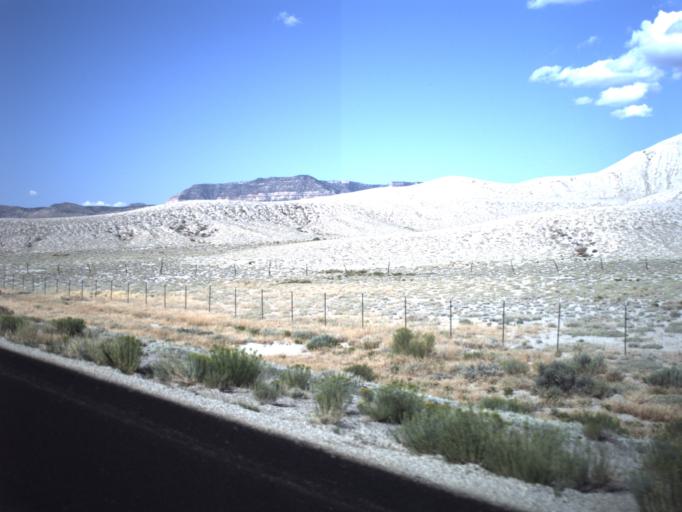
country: US
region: Utah
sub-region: Emery County
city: Ferron
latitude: 39.0026
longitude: -111.1586
